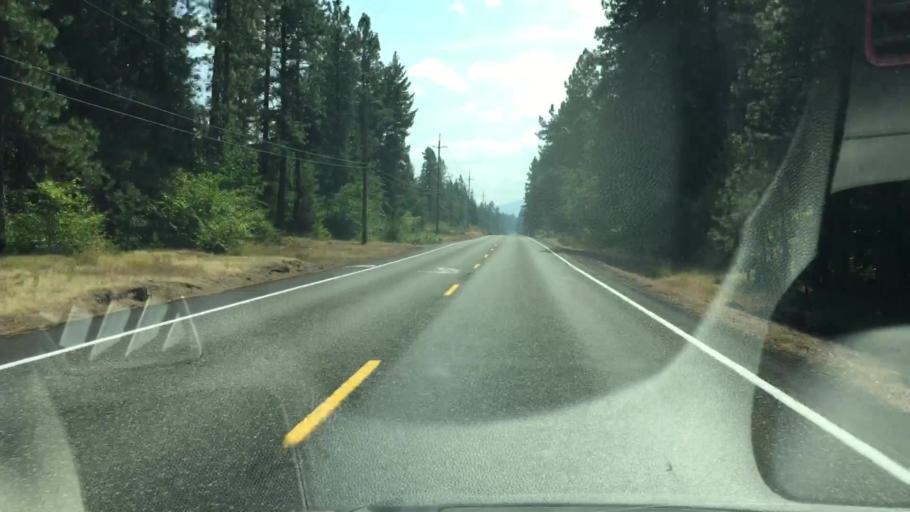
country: US
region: Washington
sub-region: Klickitat County
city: White Salmon
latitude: 45.9326
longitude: -121.4945
